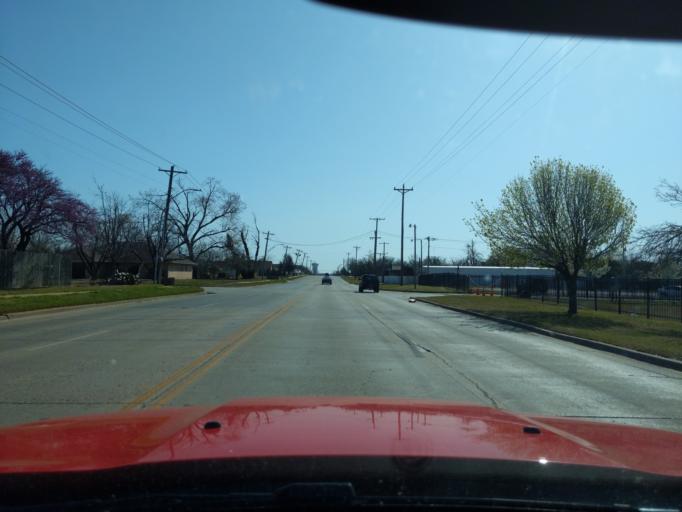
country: US
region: Oklahoma
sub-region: Cleveland County
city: Moore
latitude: 35.3488
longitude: -97.4835
